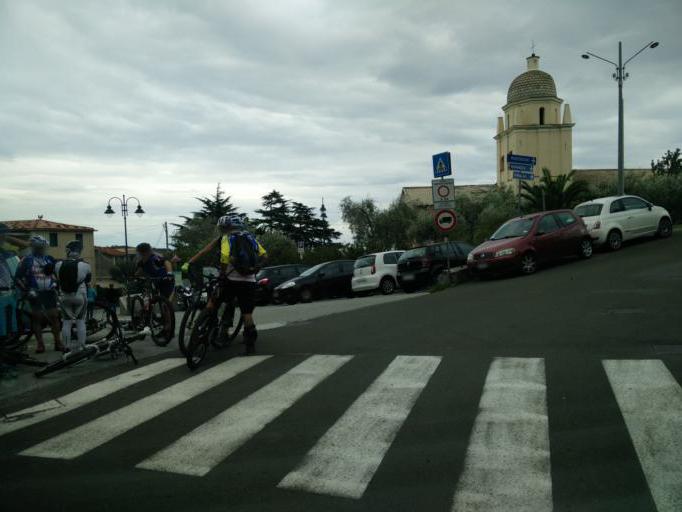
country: IT
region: Liguria
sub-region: Provincia di La Spezia
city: Riomaggiore
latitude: 44.1162
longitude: 9.7297
